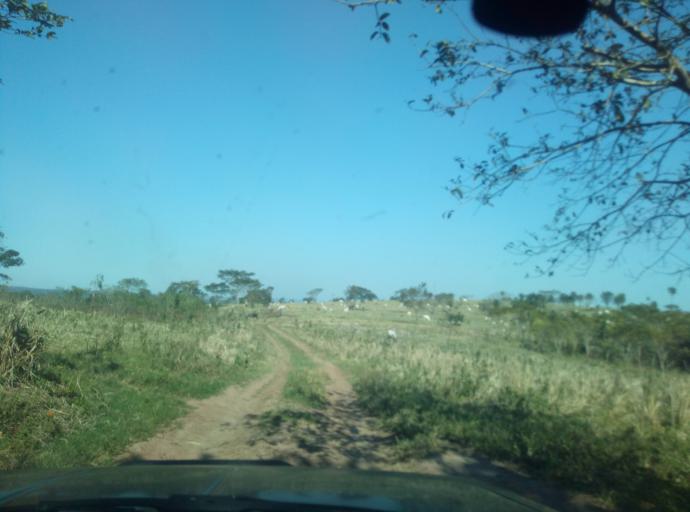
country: PY
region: Caaguazu
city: San Joaquin
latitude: -25.1740
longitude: -56.1119
